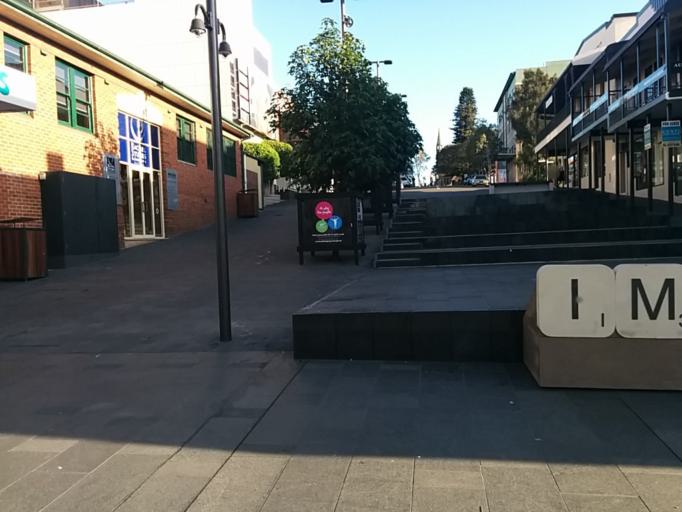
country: AU
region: New South Wales
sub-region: Wollongong
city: Wollongong
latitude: -34.4252
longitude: 150.8951
